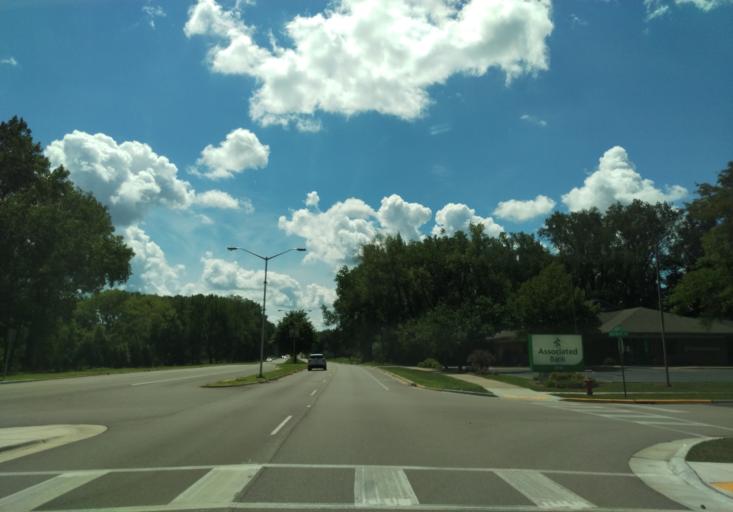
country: US
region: Wisconsin
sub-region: Dane County
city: Middleton
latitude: 43.1007
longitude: -89.4865
